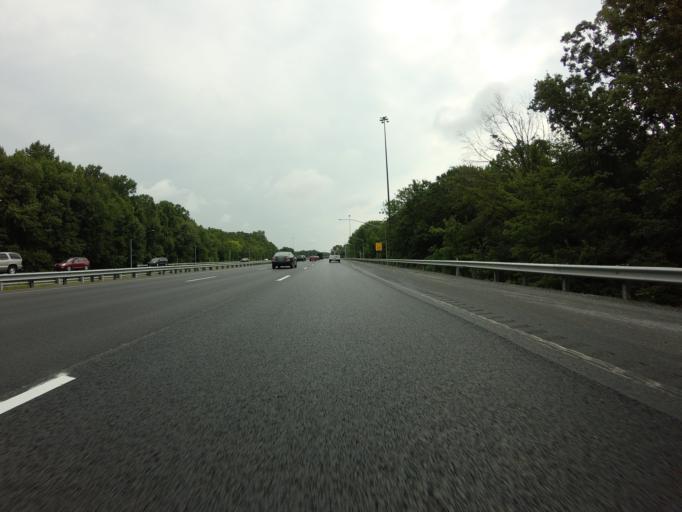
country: US
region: Maryland
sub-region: Harford County
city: Havre de Grace
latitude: 39.5659
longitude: -76.1422
